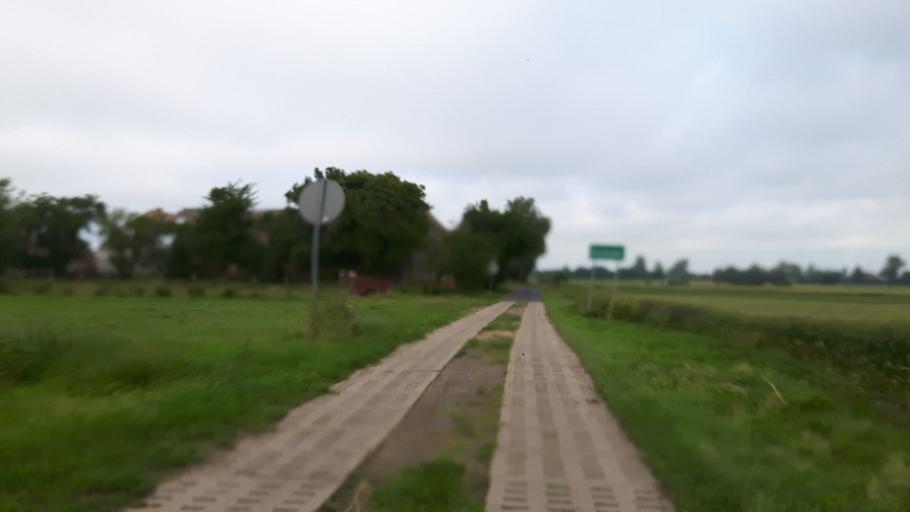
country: PL
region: West Pomeranian Voivodeship
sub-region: Powiat koszalinski
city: Sianow
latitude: 54.3100
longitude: 16.2909
